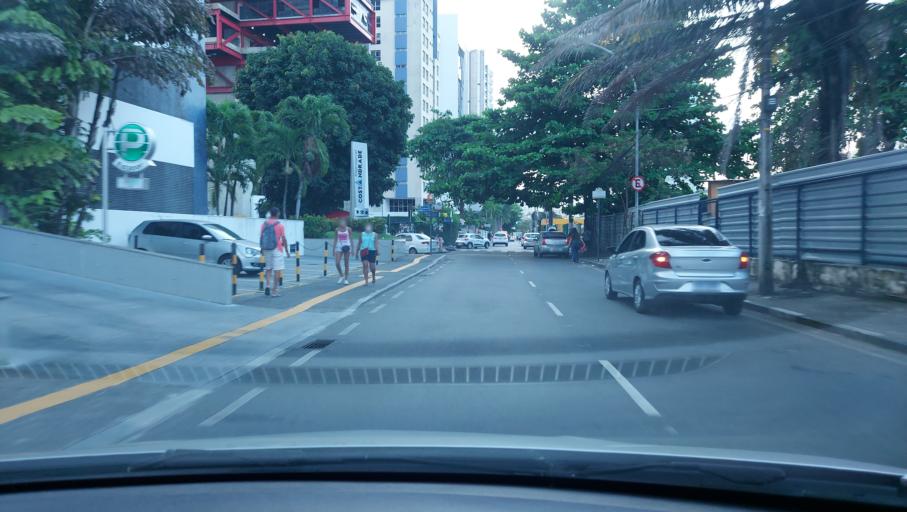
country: BR
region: Bahia
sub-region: Salvador
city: Salvador
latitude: -12.9800
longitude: -38.4551
